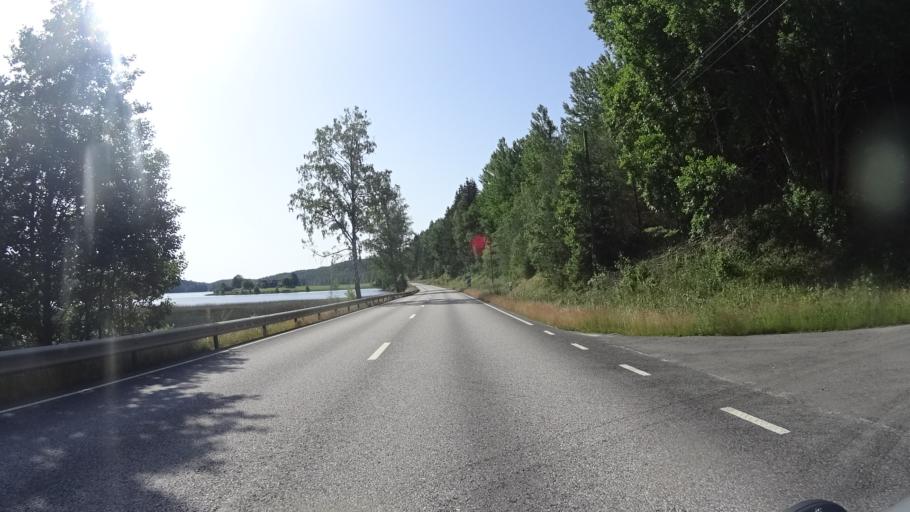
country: SE
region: Kalmar
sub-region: Vasterviks Kommun
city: Overum
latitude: 58.0080
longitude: 16.2677
